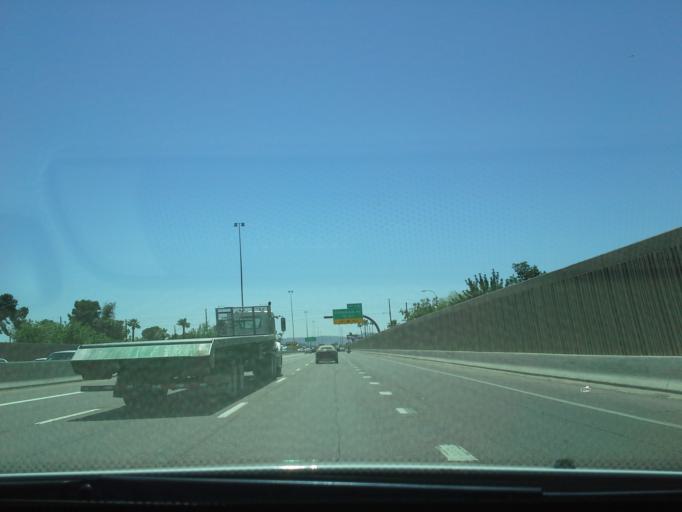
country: US
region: Arizona
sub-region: Maricopa County
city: Glendale
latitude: 33.5203
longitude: -112.1125
